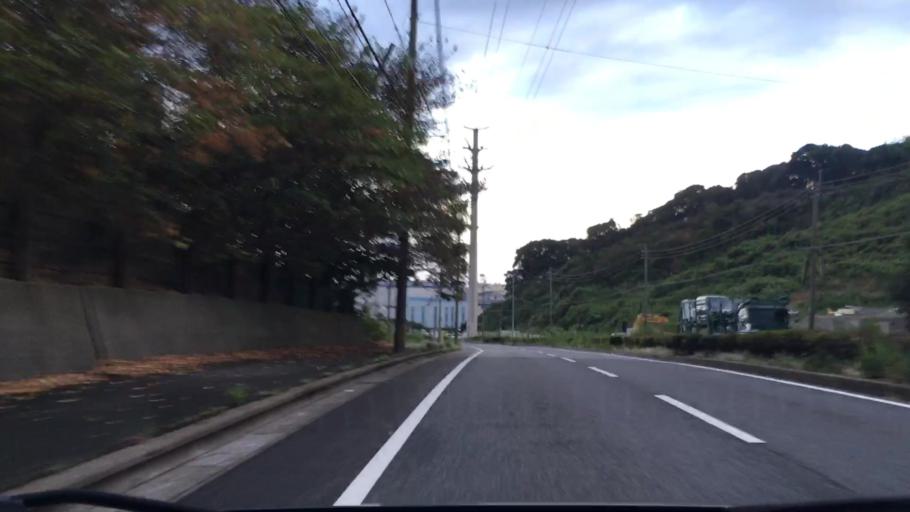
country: JP
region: Yamaguchi
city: Shimonoseki
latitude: 33.8872
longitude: 130.9816
